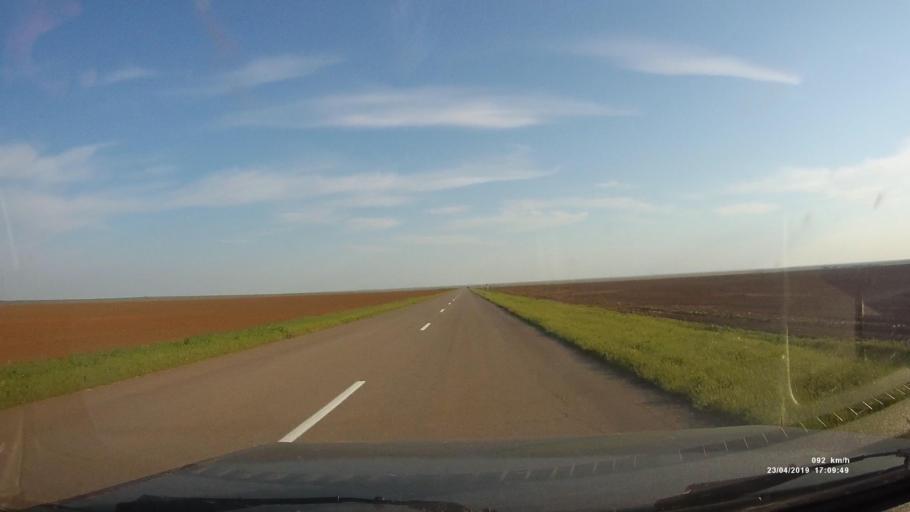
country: RU
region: Kalmykiya
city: Priyutnoye
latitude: 46.2531
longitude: 43.4842
